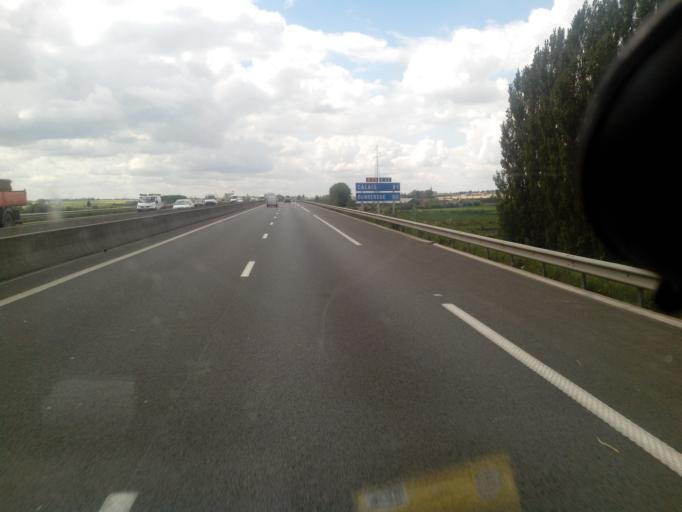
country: FR
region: Nord-Pas-de-Calais
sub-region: Departement du Nord
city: Bailleul
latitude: 50.7250
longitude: 2.7306
